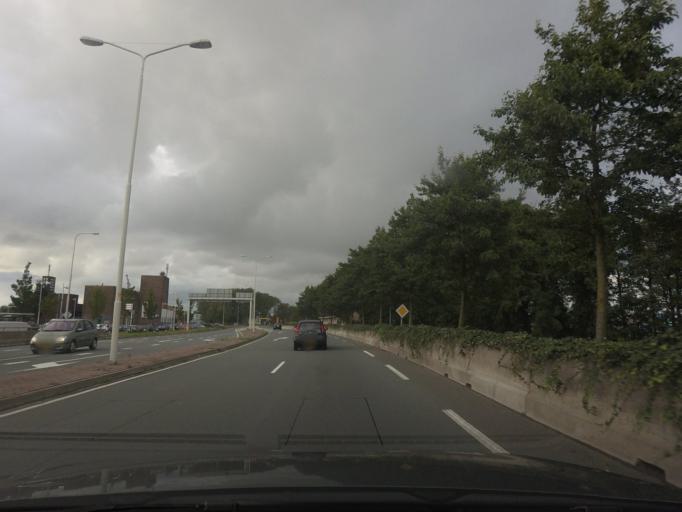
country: NL
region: North Holland
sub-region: Gemeente Uitgeest
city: Uitgeest
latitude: 52.5221
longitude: 4.7034
